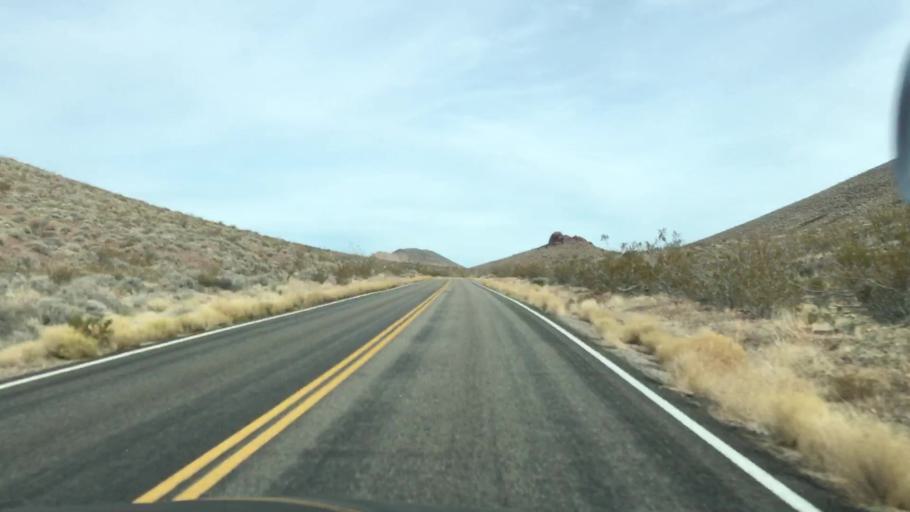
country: US
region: Nevada
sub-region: Nye County
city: Beatty
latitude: 36.7804
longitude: -116.9321
